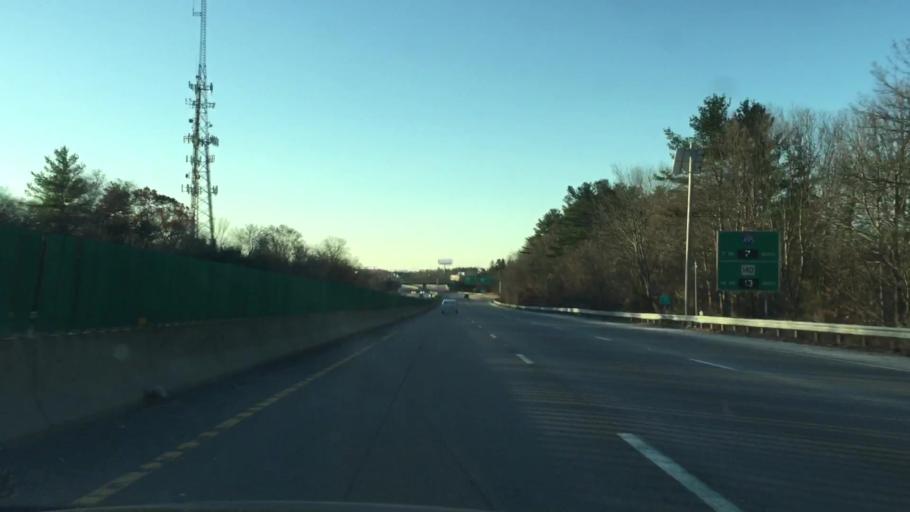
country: US
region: Massachusetts
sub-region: Plymouth County
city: Brockton
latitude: 42.0678
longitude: -71.0623
